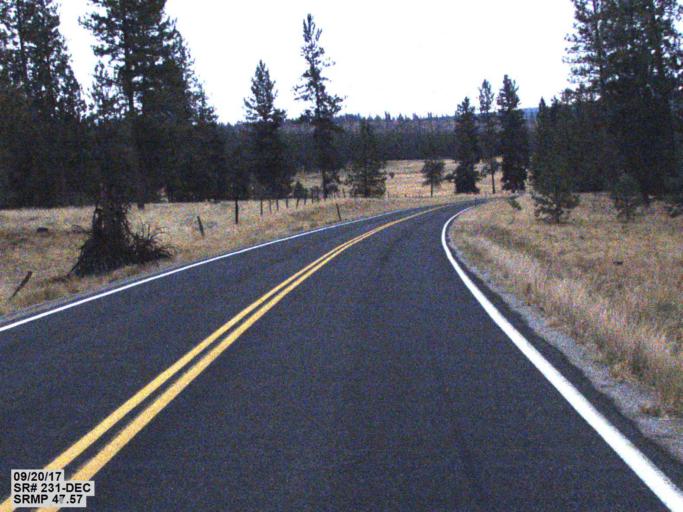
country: US
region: Washington
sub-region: Spokane County
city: Fairchild Air Force Base
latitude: 47.8764
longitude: -117.8378
